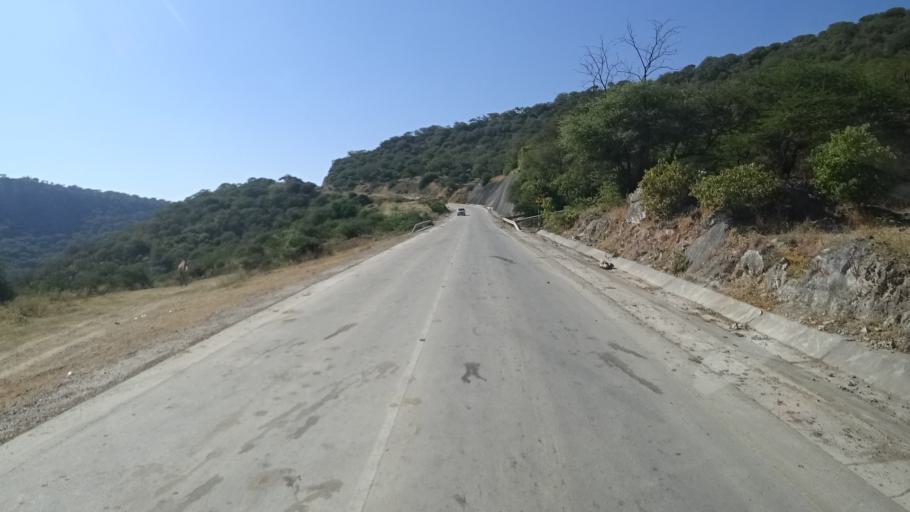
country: OM
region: Zufar
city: Salalah
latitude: 17.0604
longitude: 54.6105
